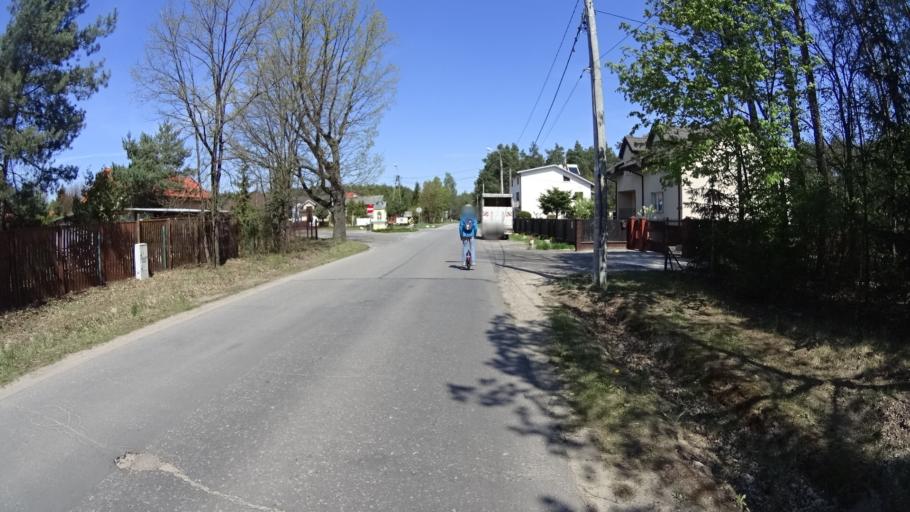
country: PL
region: Masovian Voivodeship
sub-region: Powiat warszawski zachodni
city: Truskaw
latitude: 52.2817
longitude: 20.7436
